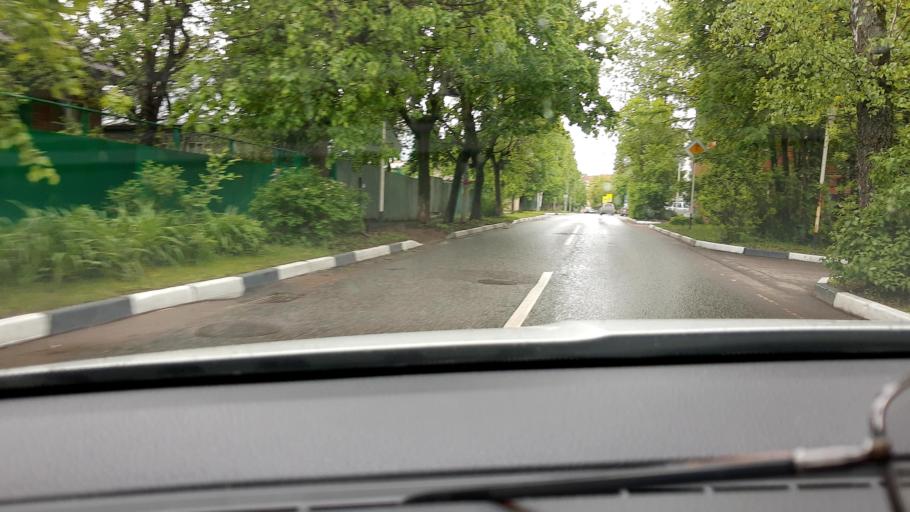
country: RU
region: Moskovskaya
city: Zvenigorod
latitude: 55.7395
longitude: 36.8678
